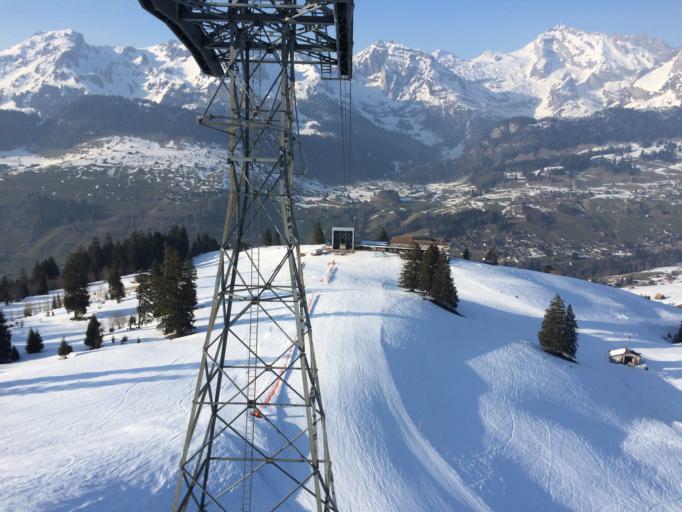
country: CH
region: Saint Gallen
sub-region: Wahlkreis Toggenburg
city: Wildhaus
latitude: 47.1818
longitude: 9.3119
